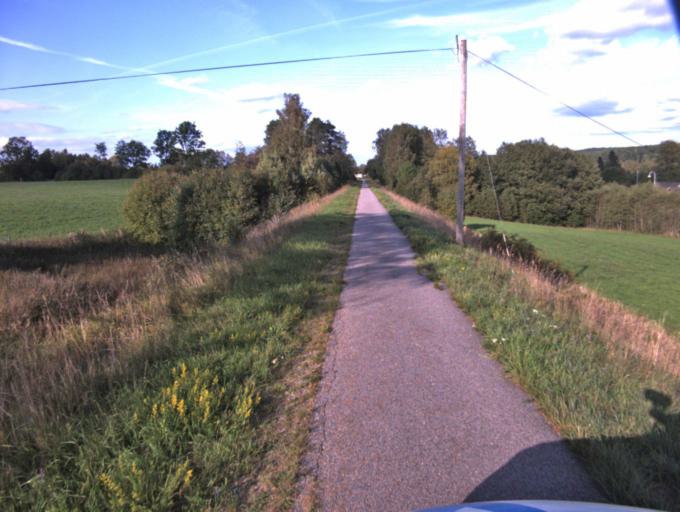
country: SE
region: Vaestra Goetaland
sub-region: Ulricehamns Kommun
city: Ulricehamn
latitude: 57.9172
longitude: 13.4846
